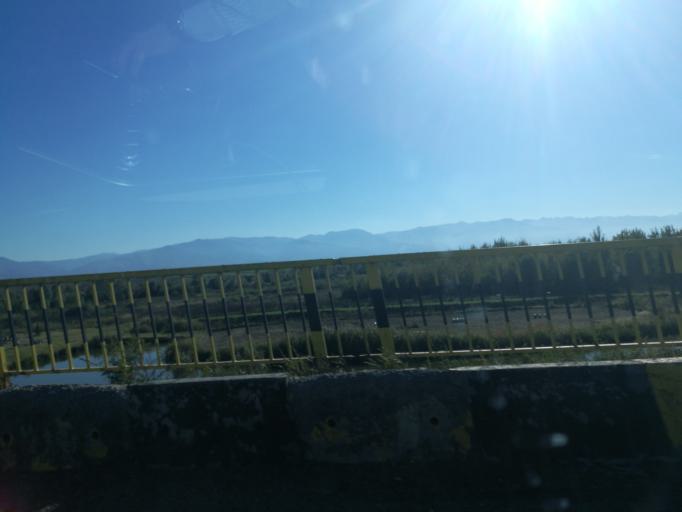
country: RO
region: Brasov
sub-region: Comuna Mandra
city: Mandra
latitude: 45.8315
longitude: 25.0169
